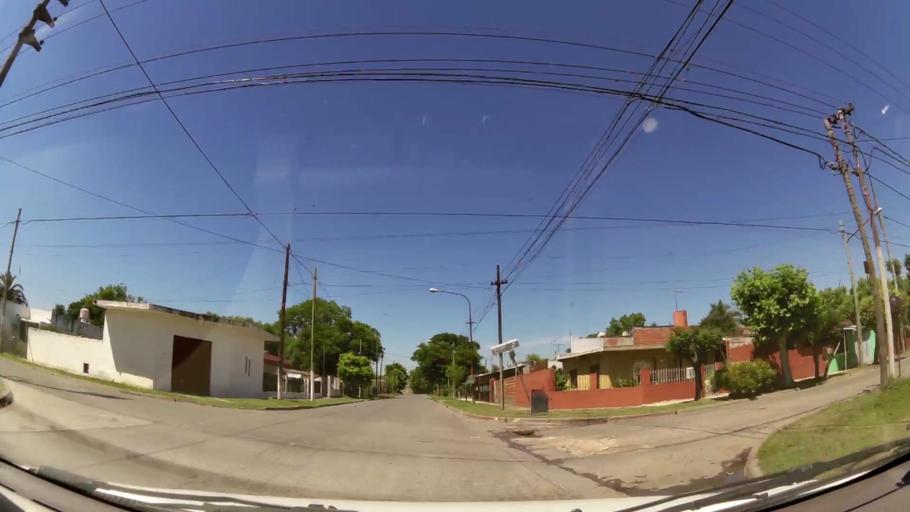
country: AR
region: Buenos Aires
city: Ituzaingo
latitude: -34.6861
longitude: -58.6611
